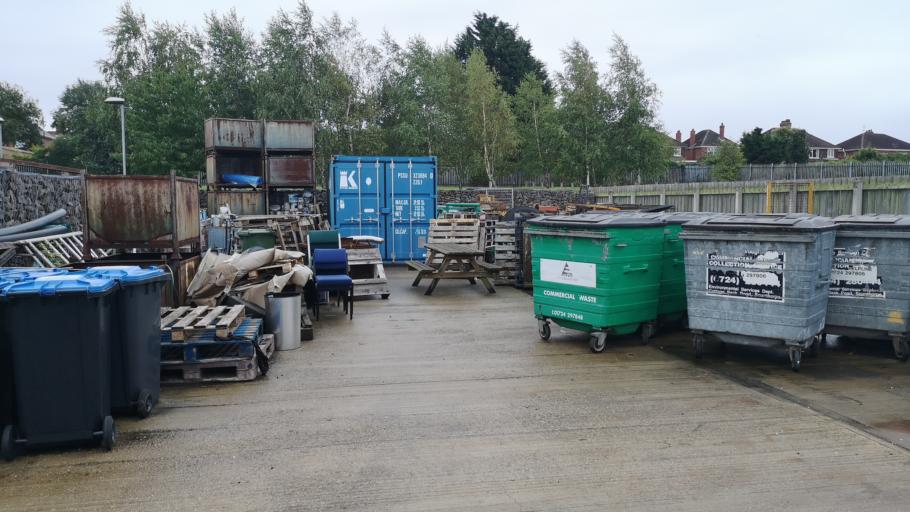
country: GB
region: England
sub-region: North Lincolnshire
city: Scunthorpe
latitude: 53.5770
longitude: -0.6669
